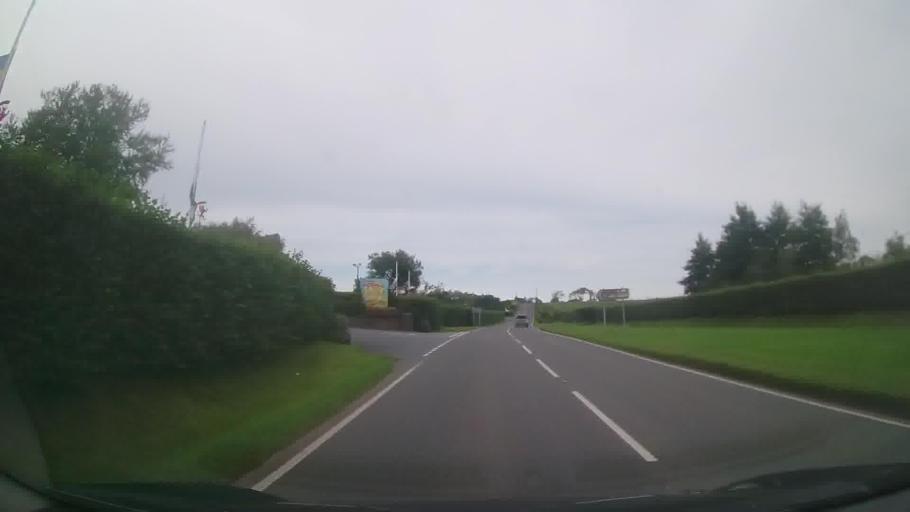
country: GB
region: Wales
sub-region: Pembrokeshire
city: Kilgetty
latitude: 51.7449
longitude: -4.7302
